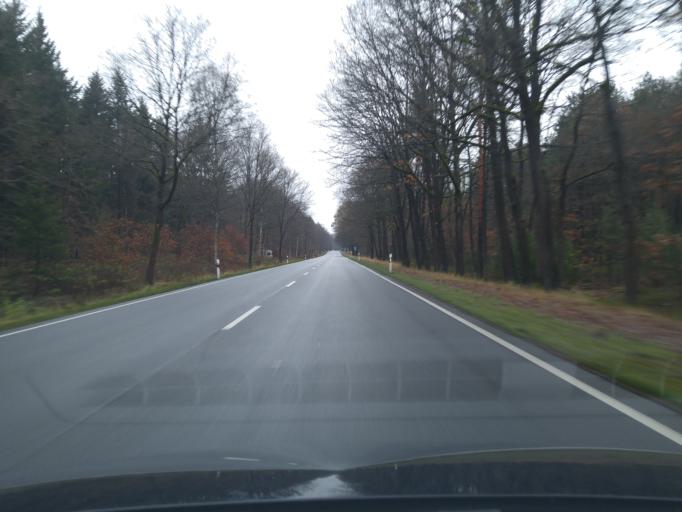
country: DE
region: Lower Saxony
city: Sprakensehl
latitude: 52.8027
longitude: 10.4880
